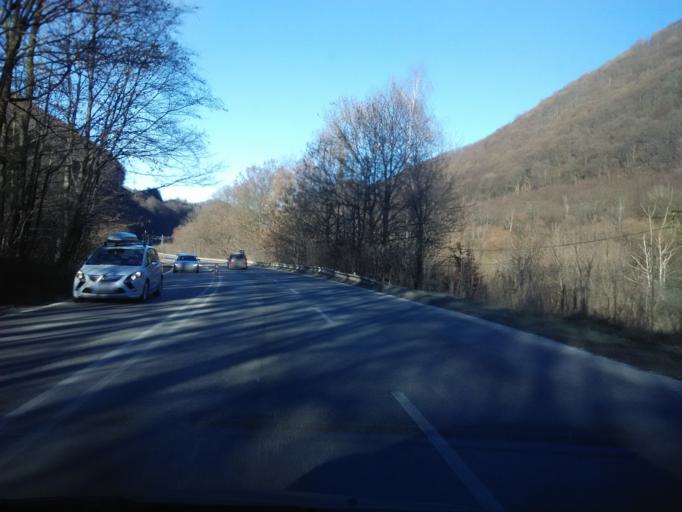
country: SK
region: Zilinsky
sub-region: Okres Zilina
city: Vrutky
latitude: 49.1412
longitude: 18.8921
